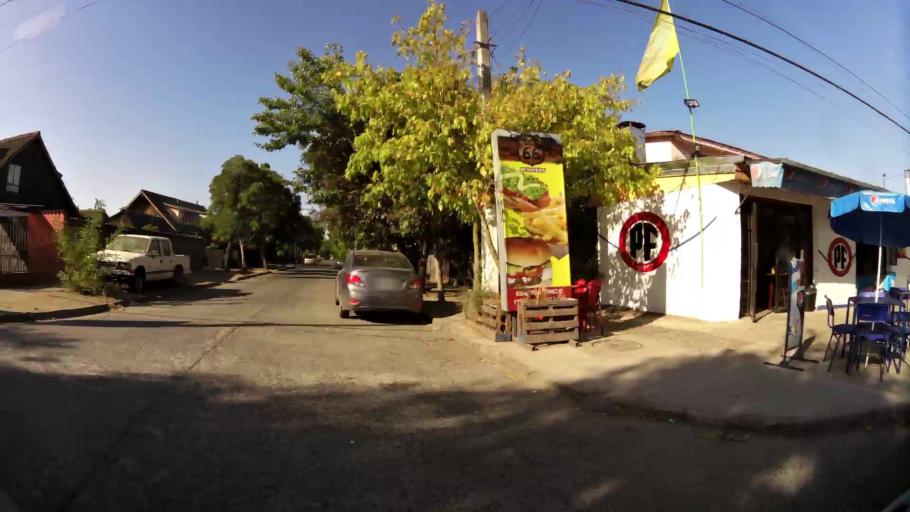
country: CL
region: Maule
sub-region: Provincia de Talca
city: Talca
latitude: -35.4431
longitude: -71.6724
